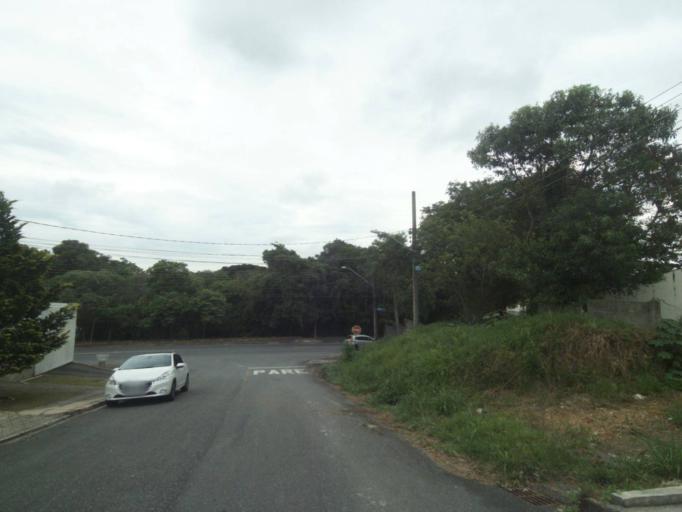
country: BR
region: Parana
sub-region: Curitiba
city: Curitiba
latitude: -25.4019
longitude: -49.2930
